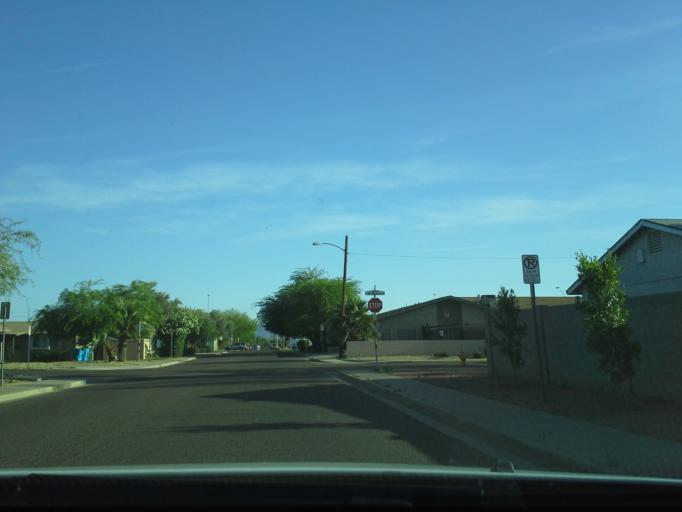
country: US
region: Arizona
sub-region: Maricopa County
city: Phoenix
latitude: 33.4670
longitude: -112.0521
